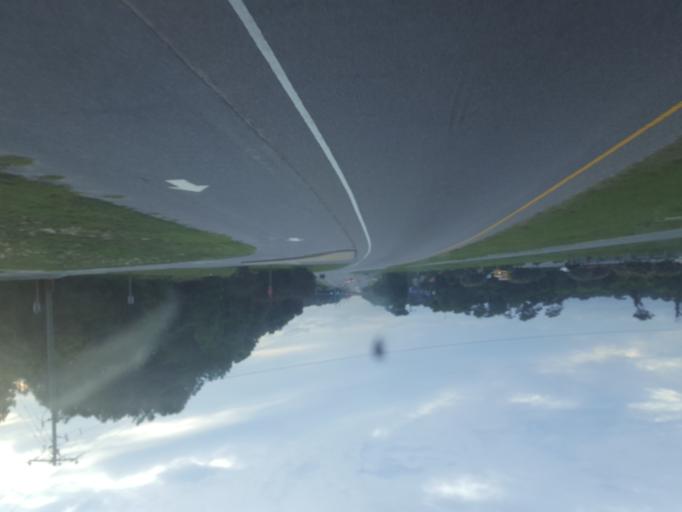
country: US
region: North Carolina
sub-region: Dare County
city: Kitty Hawk
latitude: 36.0999
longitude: -75.7167
